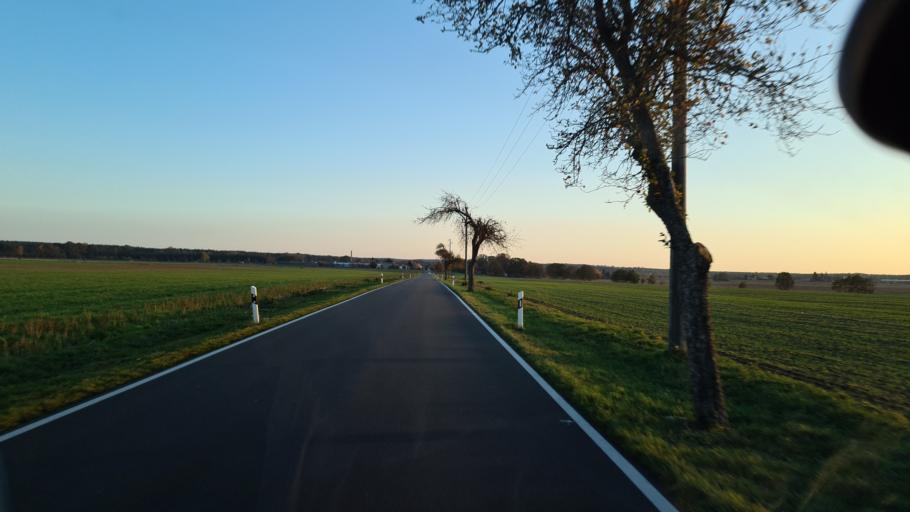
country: DE
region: Saxony
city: Torgau
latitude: 51.4831
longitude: 13.0042
